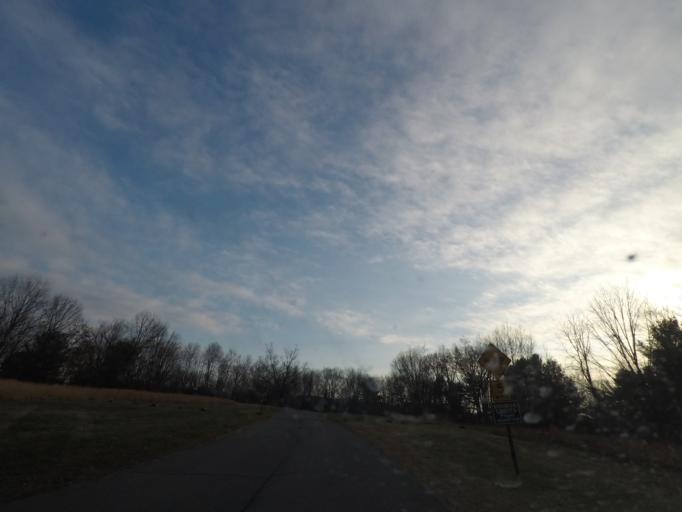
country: US
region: New York
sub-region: Rensselaer County
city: Wynantskill
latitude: 42.7254
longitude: -73.6495
